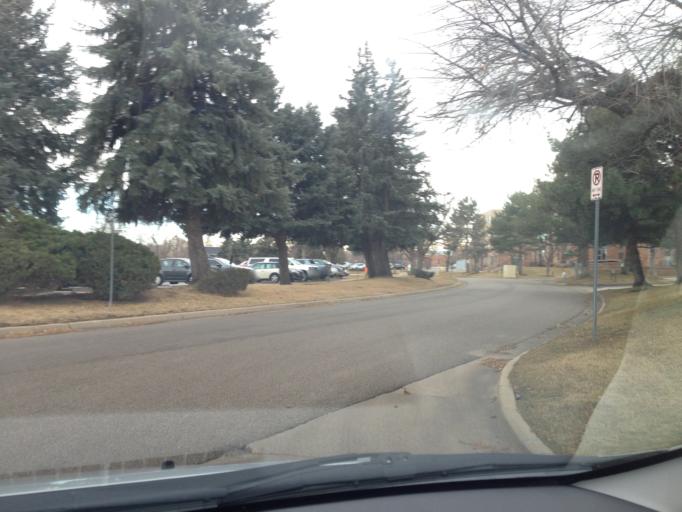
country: US
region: Colorado
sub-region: Boulder County
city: Boulder
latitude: 40.0167
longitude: -105.2469
